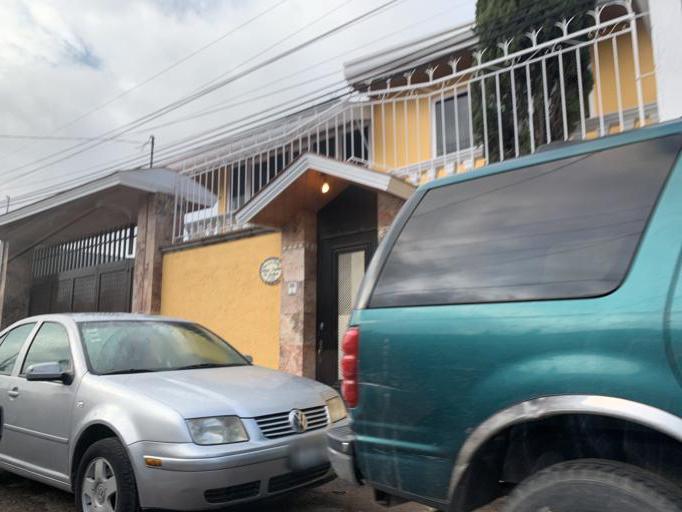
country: MX
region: Puebla
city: Cholula
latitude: 19.0739
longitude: -98.3136
